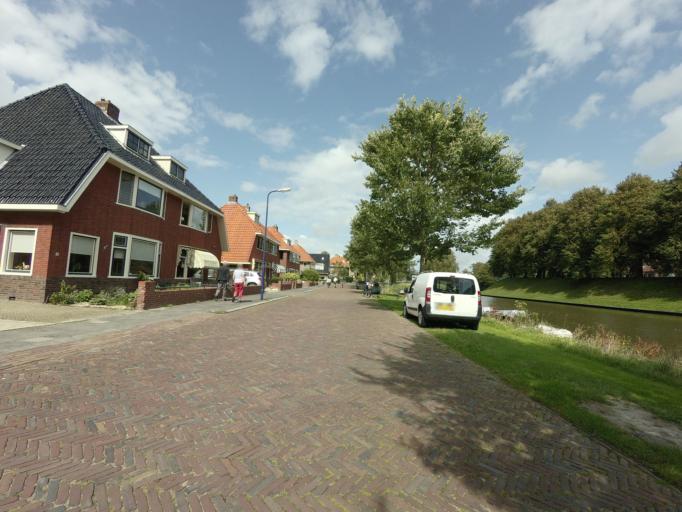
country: NL
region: Friesland
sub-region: Gemeente Franekeradeel
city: Franeker
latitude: 53.1878
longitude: 5.5379
